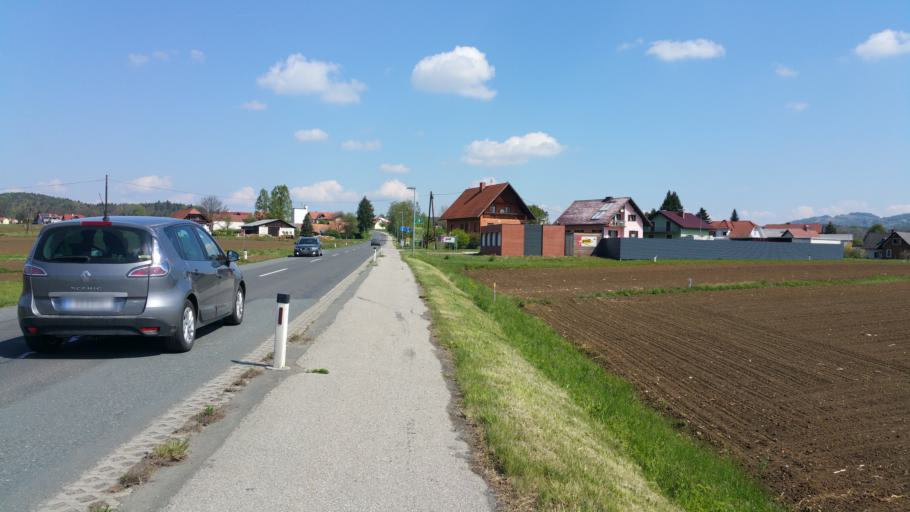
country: AT
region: Styria
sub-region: Politischer Bezirk Leibnitz
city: Gleinstatten
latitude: 46.7597
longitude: 15.3725
